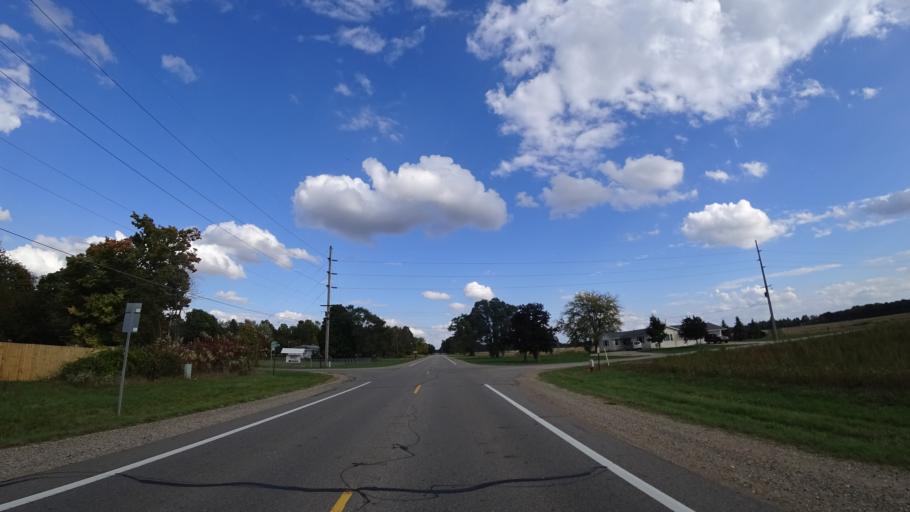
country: US
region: Michigan
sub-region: Saint Joseph County
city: Three Rivers
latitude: 41.9546
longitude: -85.6062
